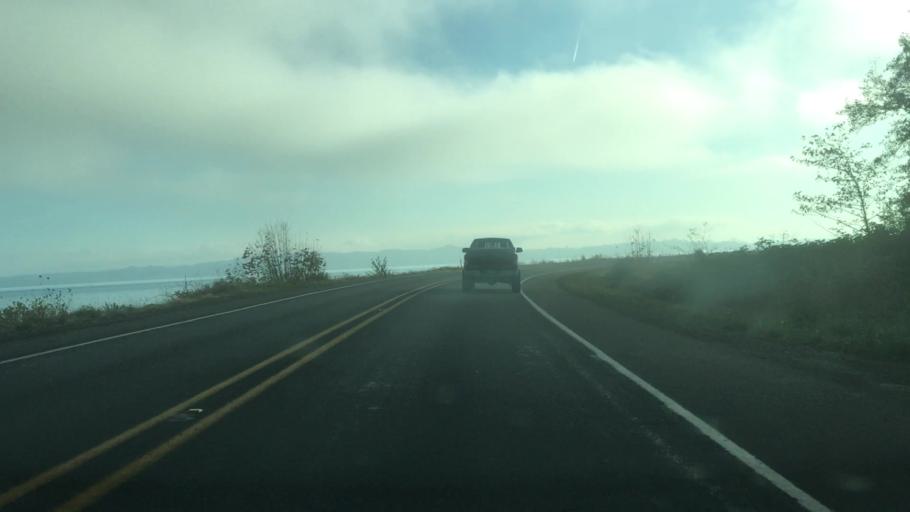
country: US
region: Oregon
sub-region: Clatsop County
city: Astoria
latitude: 46.2723
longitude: -123.8164
